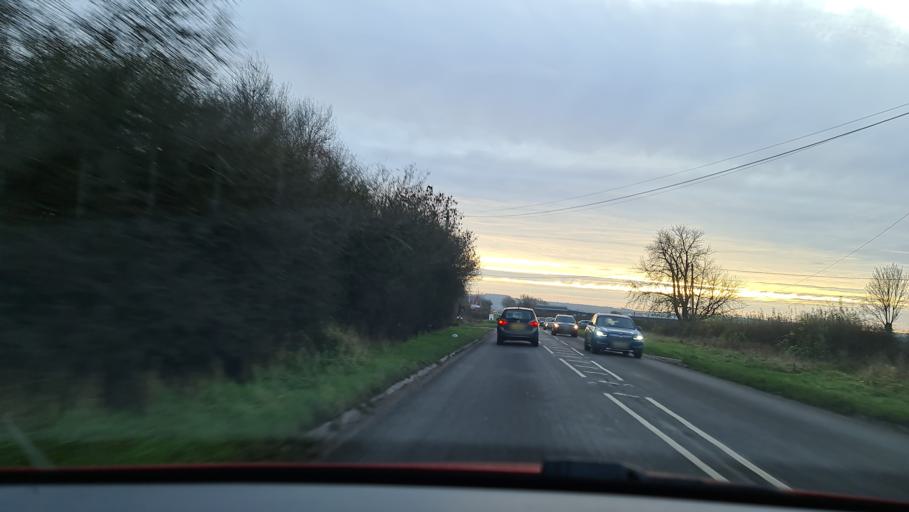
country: GB
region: England
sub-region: Buckinghamshire
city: Princes Risborough
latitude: 51.7496
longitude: -0.8769
